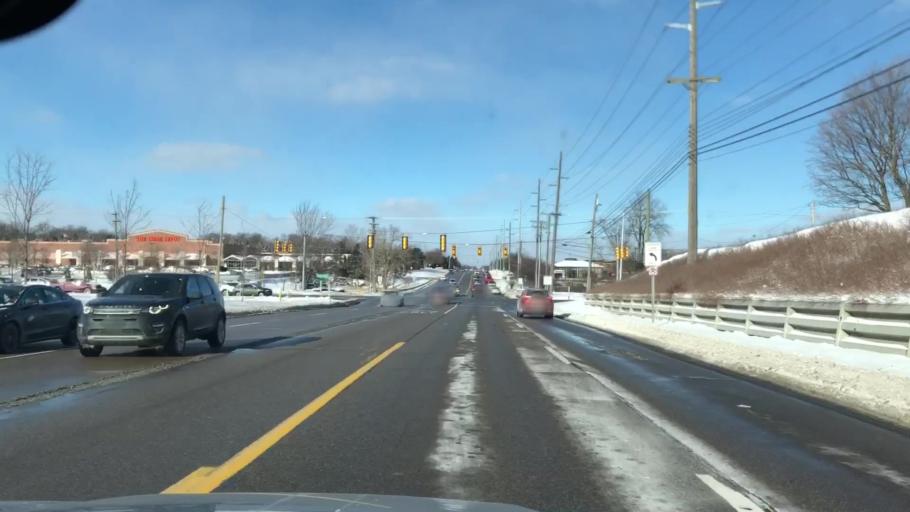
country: US
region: Michigan
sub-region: Wayne County
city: Northville
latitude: 42.4241
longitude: -83.4330
